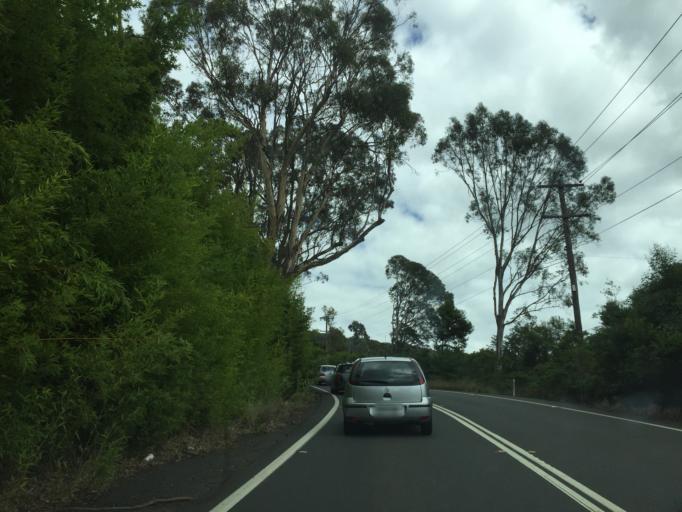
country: AU
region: New South Wales
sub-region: Hawkesbury
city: Richmond
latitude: -33.5449
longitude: 150.6481
